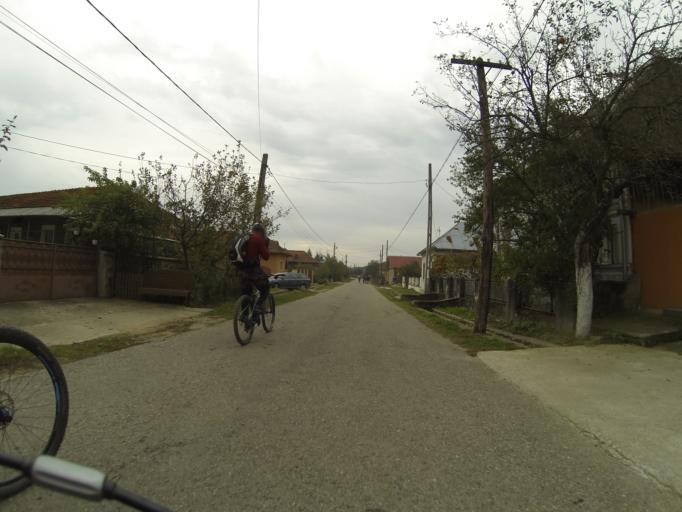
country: RO
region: Gorj
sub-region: Comuna Tismana
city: Pocruia
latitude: 45.0463
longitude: 22.9222
